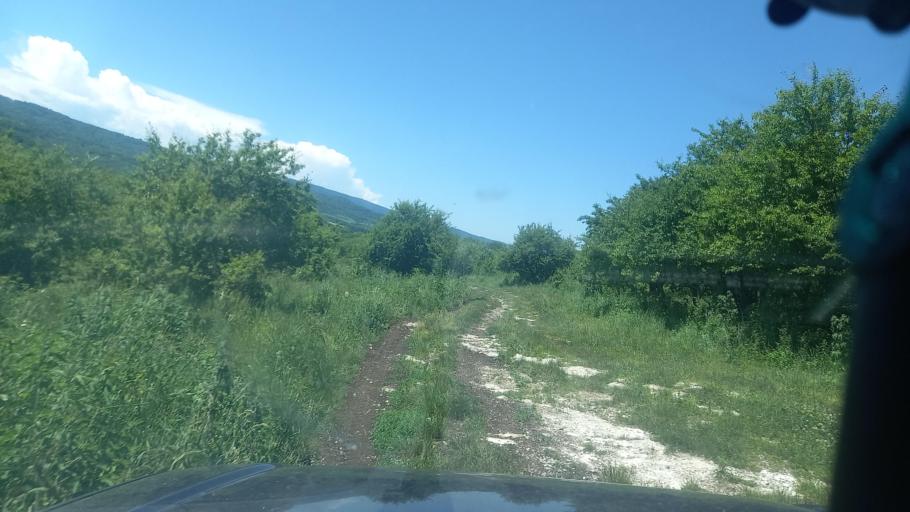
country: RU
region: Karachayevo-Cherkesiya
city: Pregradnaya
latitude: 44.1054
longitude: 41.1307
